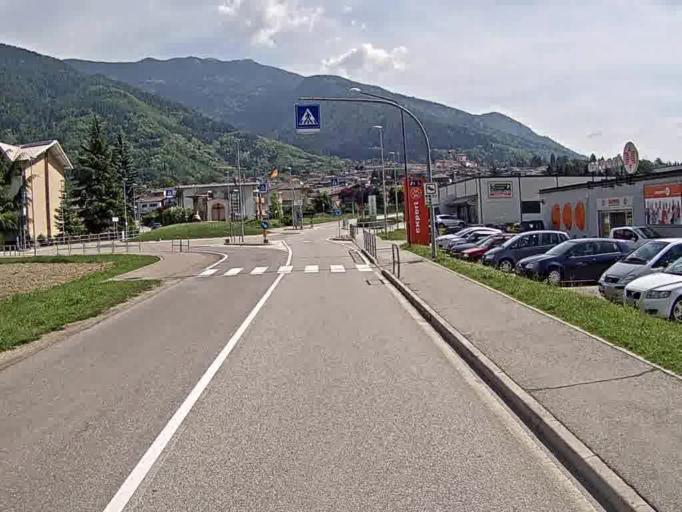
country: IT
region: Trentino-Alto Adige
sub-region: Provincia di Trento
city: Levico Terme
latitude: 46.0068
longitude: 11.2925
